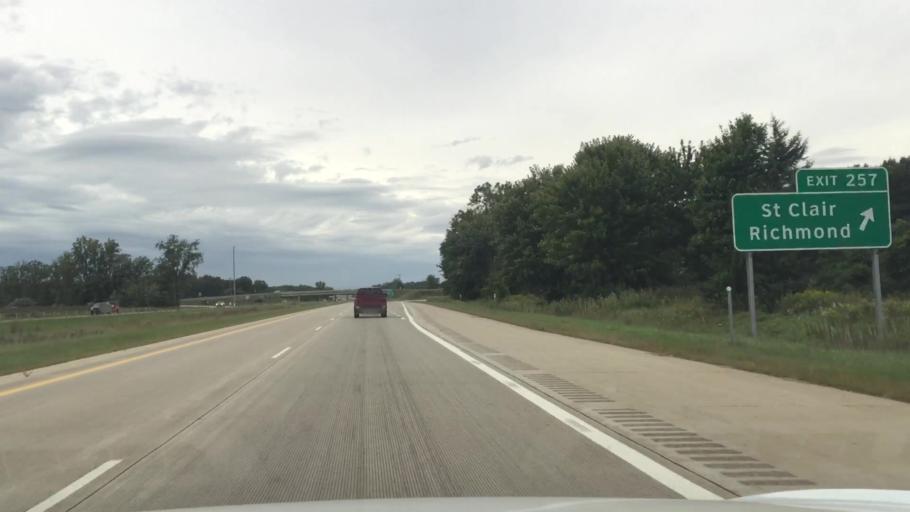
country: US
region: Michigan
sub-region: Macomb County
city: Richmond
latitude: 42.8169
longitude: -82.6225
